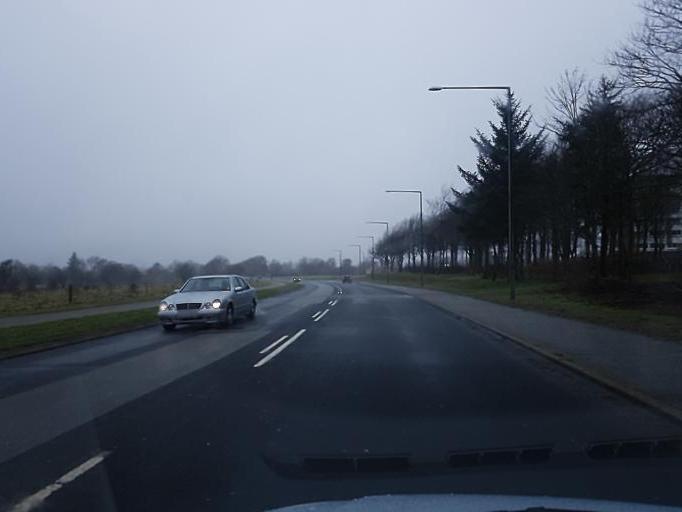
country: DK
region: South Denmark
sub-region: Esbjerg Kommune
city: Esbjerg
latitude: 55.4925
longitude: 8.4846
